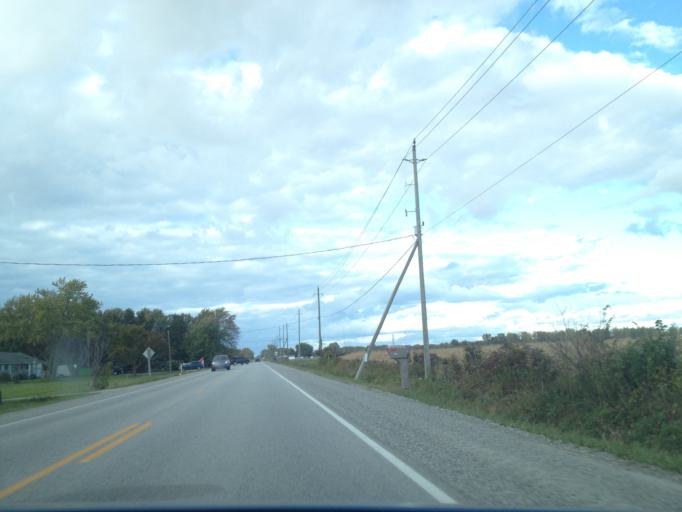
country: US
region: Michigan
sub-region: Wayne County
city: Grosse Pointe Farms
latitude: 42.2751
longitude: -82.7130
